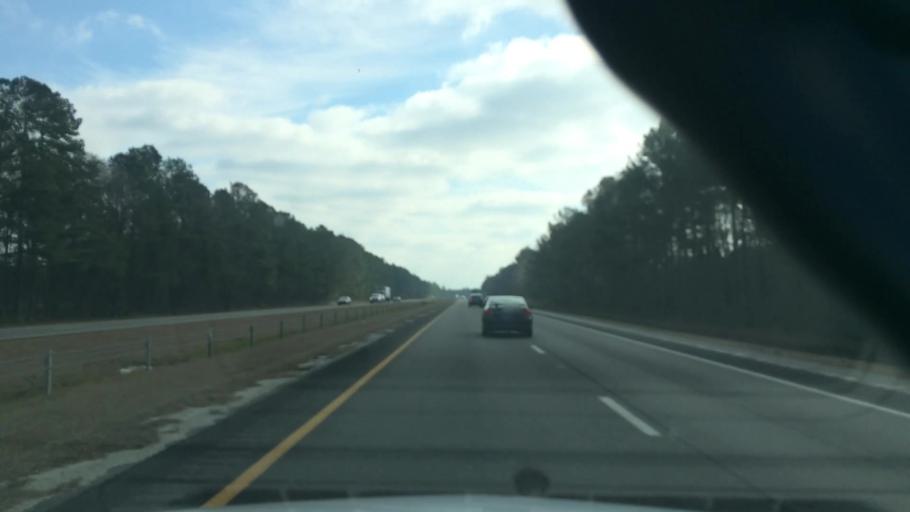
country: US
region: North Carolina
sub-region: Pender County
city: Burgaw
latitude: 34.5990
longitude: -77.9122
